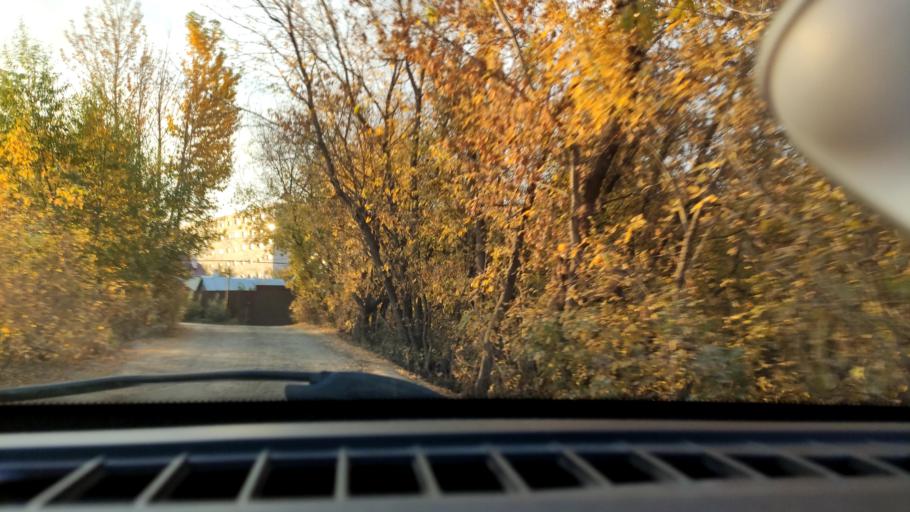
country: RU
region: Samara
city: Samara
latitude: 53.2692
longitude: 50.2288
